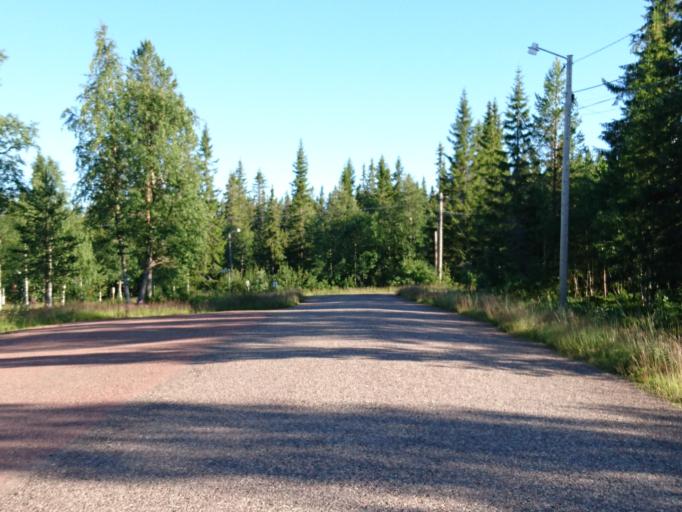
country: SE
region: Dalarna
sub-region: Malung-Saelens kommun
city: Malung
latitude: 61.1712
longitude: 13.1765
